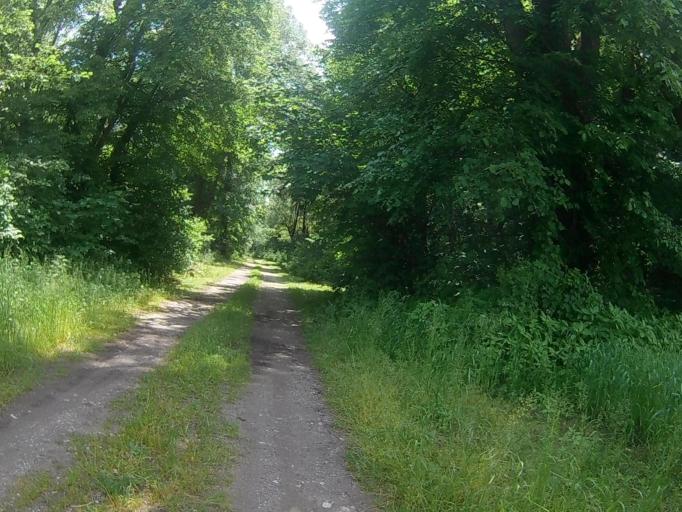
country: SI
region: Starse
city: Starse
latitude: 46.4708
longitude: 15.7708
